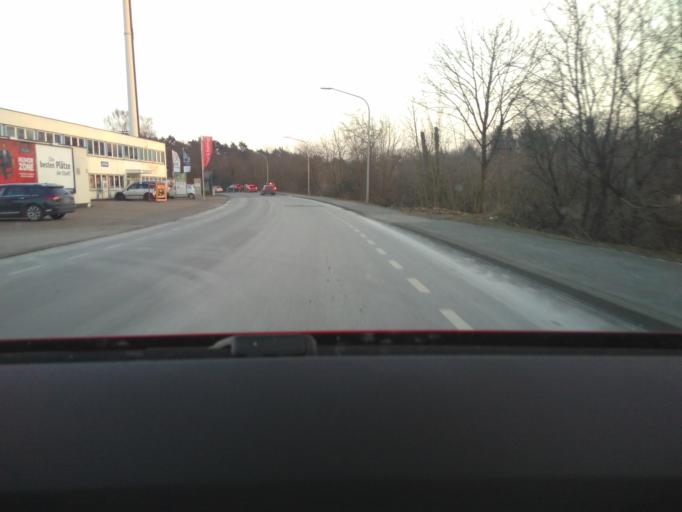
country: DE
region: North Rhine-Westphalia
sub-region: Regierungsbezirk Detmold
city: Verl
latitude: 51.9488
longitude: 8.5706
